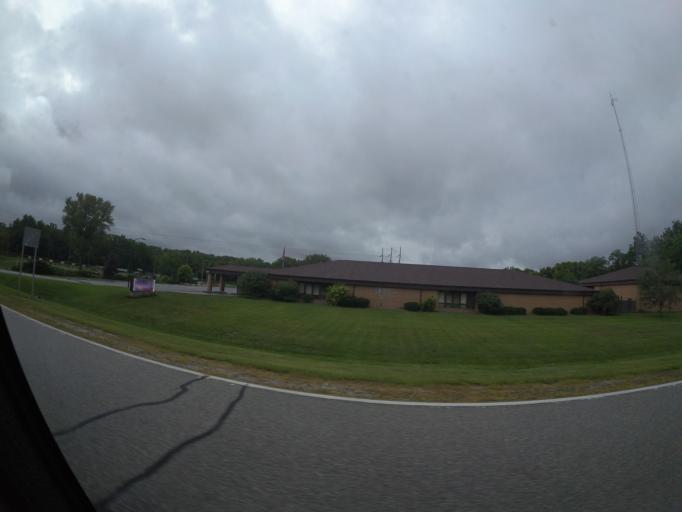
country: US
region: Indiana
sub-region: Montgomery County
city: Crawfordsville
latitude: 40.0516
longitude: -86.9025
